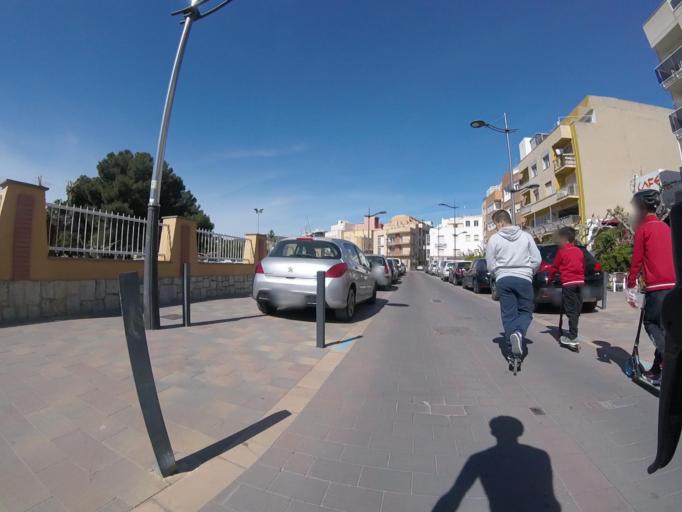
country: ES
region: Valencia
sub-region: Provincia de Castello
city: Peniscola
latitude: 40.3592
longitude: 0.4043
